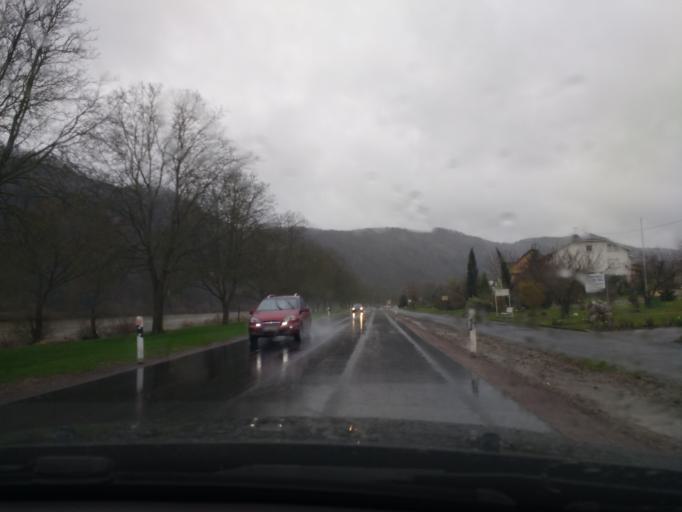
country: DE
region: Rheinland-Pfalz
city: Krov
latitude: 49.9746
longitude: 7.0861
